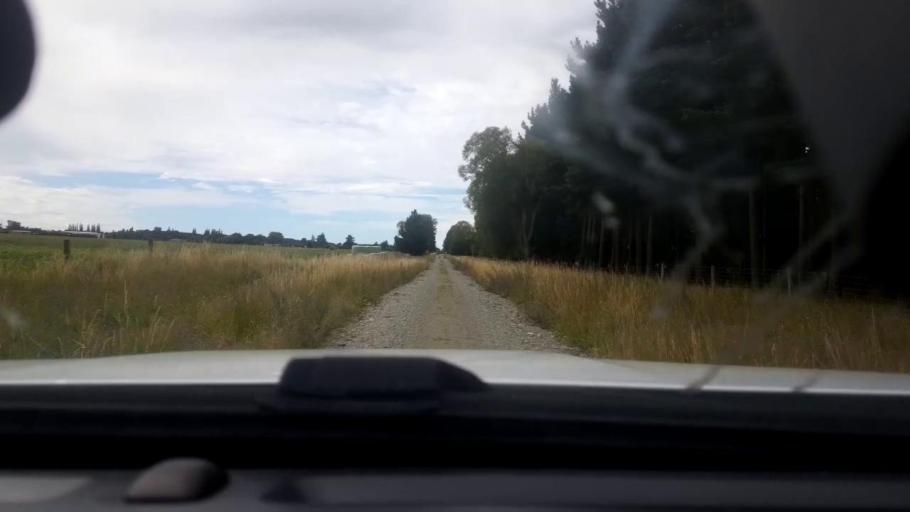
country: NZ
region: Canterbury
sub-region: Timaru District
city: Pleasant Point
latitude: -44.1325
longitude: 171.2818
